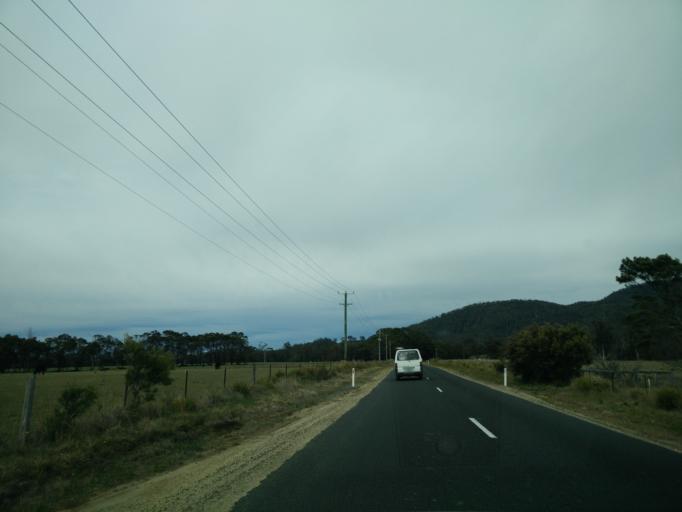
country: AU
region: Tasmania
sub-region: Break O'Day
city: St Helens
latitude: -41.8933
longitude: 148.2632
